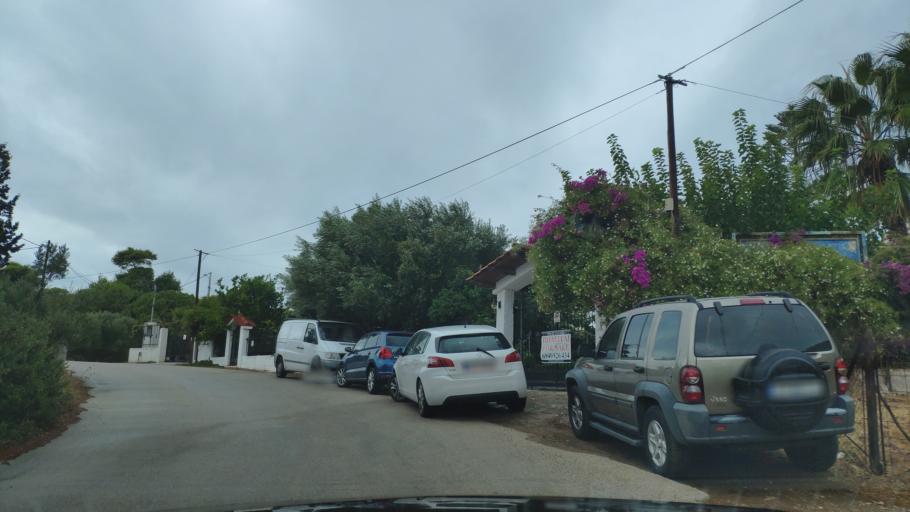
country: GR
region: Peloponnese
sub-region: Nomos Korinthias
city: Perachora
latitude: 38.0330
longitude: 22.8728
